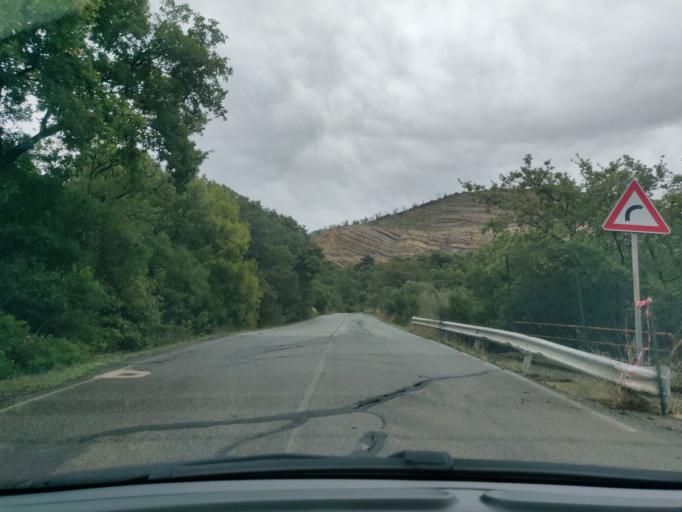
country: IT
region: Latium
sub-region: Citta metropolitana di Roma Capitale
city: Allumiere
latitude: 42.1290
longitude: 11.8537
